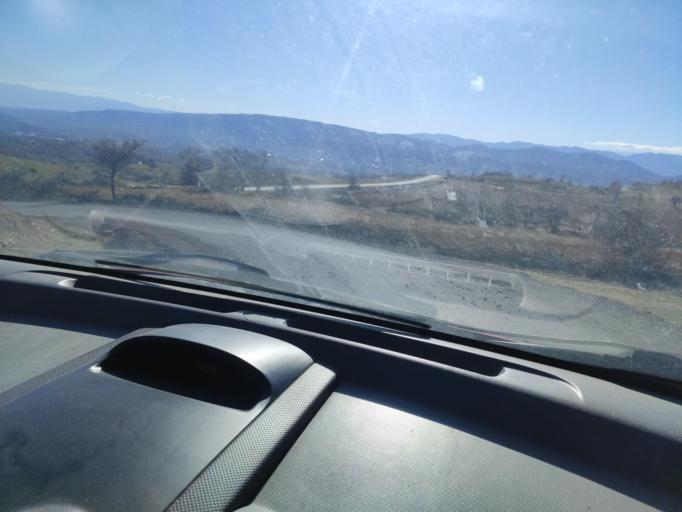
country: MK
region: Radovis
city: Radovish
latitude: 41.6594
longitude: 22.4095
